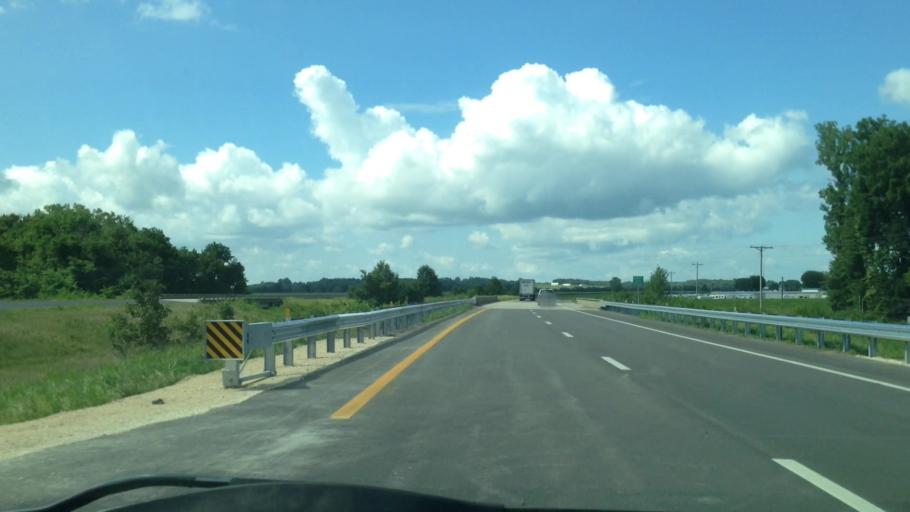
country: US
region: Illinois
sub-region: Adams County
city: Quincy
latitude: 39.9818
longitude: -91.5255
